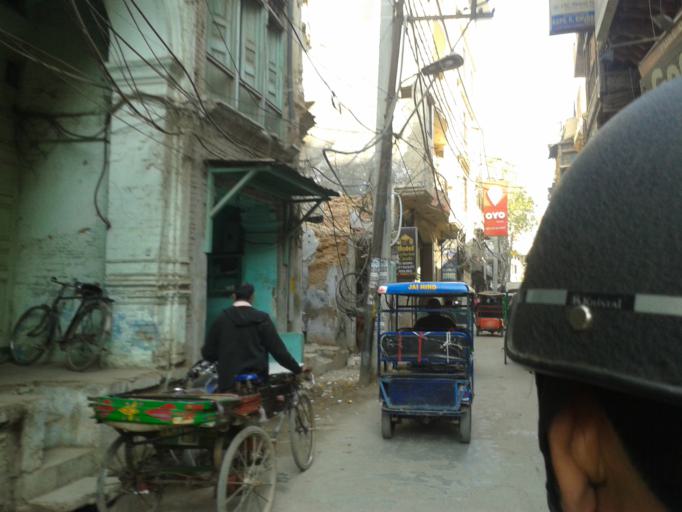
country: IN
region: Punjab
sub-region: Amritsar
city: Amritsar
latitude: 31.6224
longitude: 74.8783
